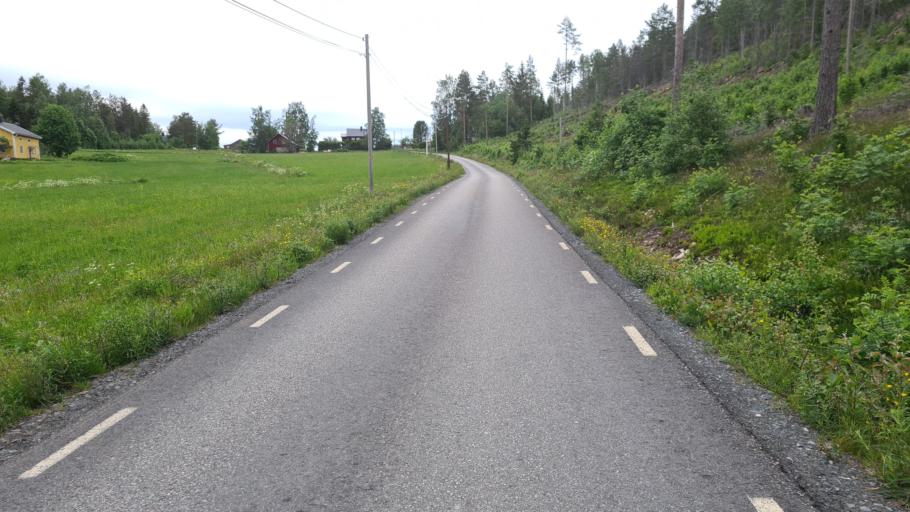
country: SE
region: Vaesternorrland
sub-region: Kramfors Kommun
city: Nordingra
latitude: 62.9774
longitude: 18.4279
